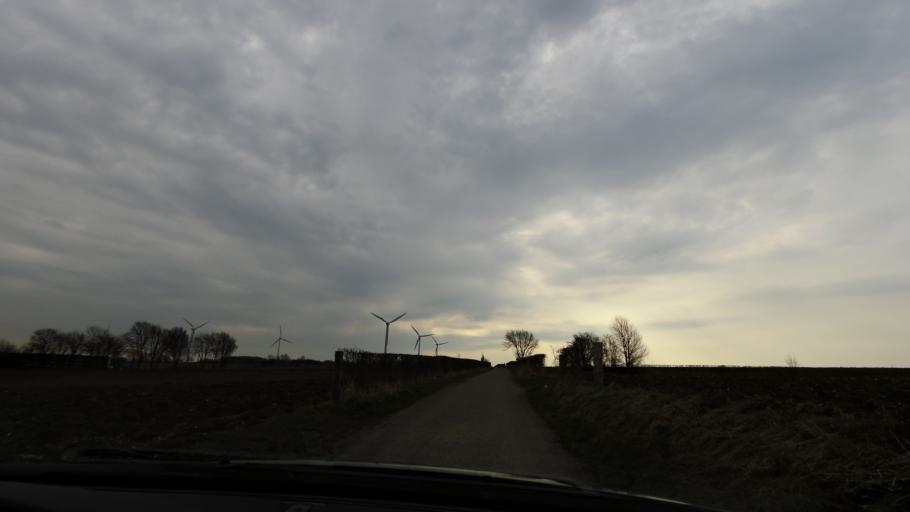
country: NL
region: Limburg
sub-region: Gemeente Simpelveld
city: Simpelveld
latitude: 50.8119
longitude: 6.0089
